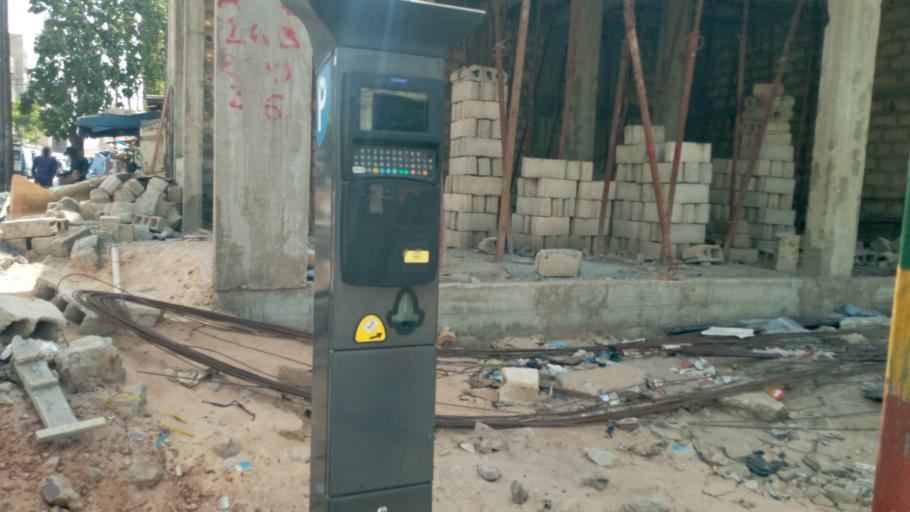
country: SN
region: Dakar
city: Dakar
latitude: 14.6822
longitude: -17.4480
